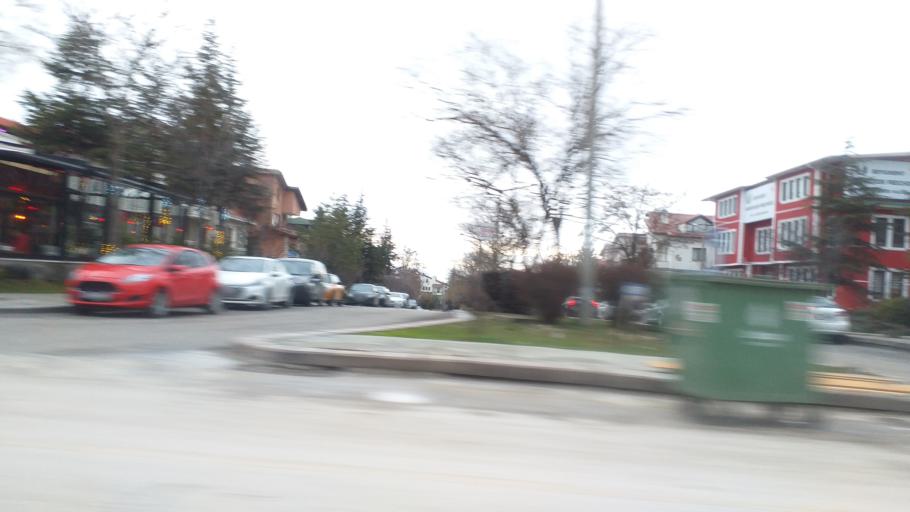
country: TR
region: Ankara
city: Batikent
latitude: 39.8914
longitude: 32.7230
